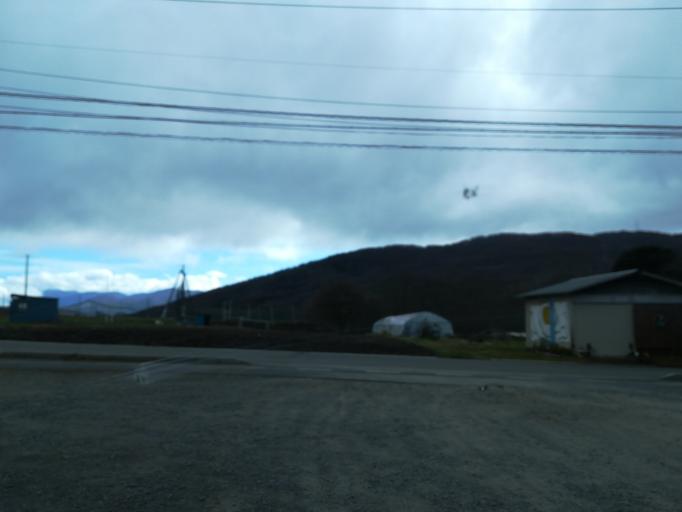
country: JP
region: Nagano
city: Suzaka
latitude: 36.5265
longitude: 138.3260
